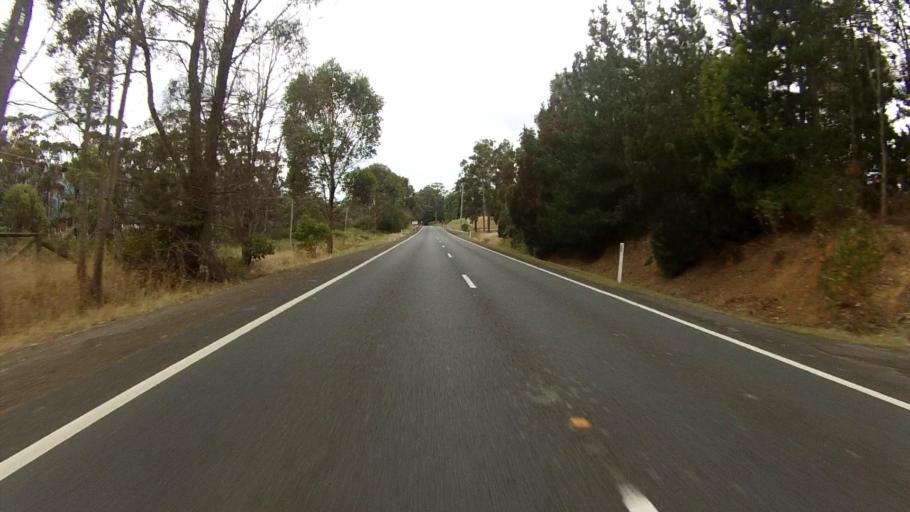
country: AU
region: Tasmania
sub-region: Huon Valley
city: Franklin
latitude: -43.0809
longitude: 147.0316
